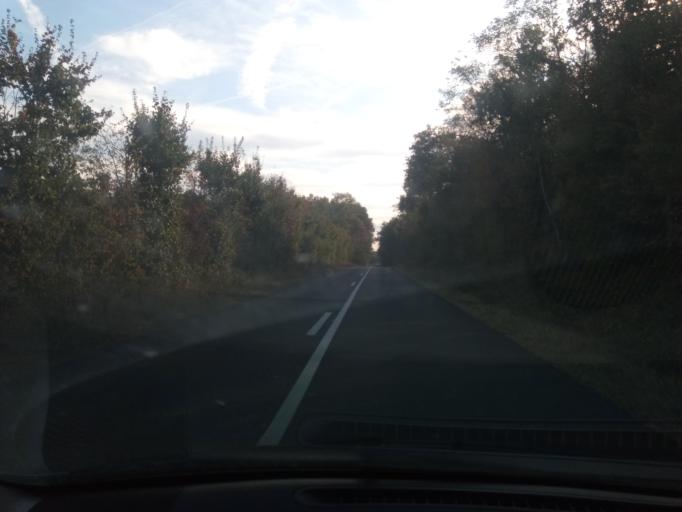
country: FR
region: Poitou-Charentes
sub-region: Departement de la Vienne
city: Saint-Savin
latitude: 46.5000
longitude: 0.8458
